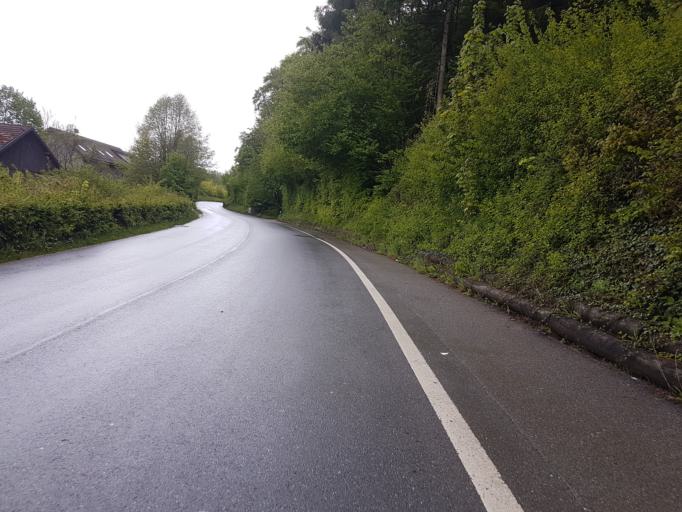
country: CH
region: Vaud
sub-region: Gros-de-Vaud District
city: Penthalaz
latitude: 46.5999
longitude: 6.5252
